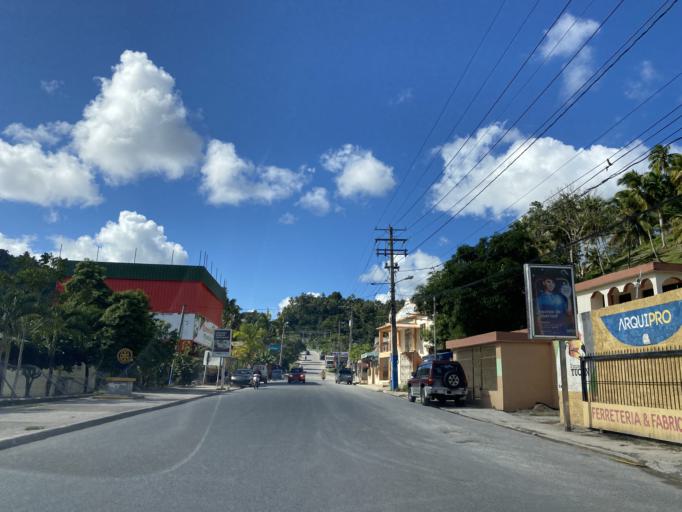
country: DO
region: Samana
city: Samana
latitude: 19.2060
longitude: -69.3470
